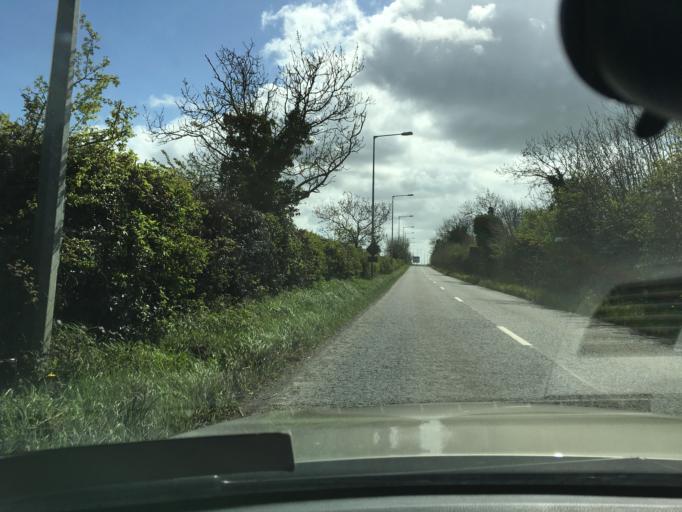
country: IE
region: Leinster
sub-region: Fingal County
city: Blanchardstown
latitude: 53.4261
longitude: -6.3682
